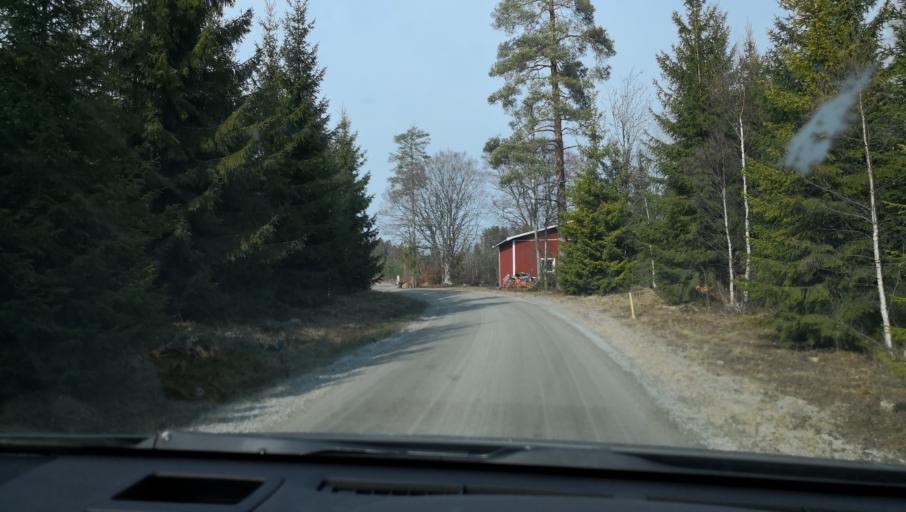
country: SE
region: OErebro
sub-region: Lindesbergs Kommun
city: Frovi
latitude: 59.3629
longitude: 15.4330
